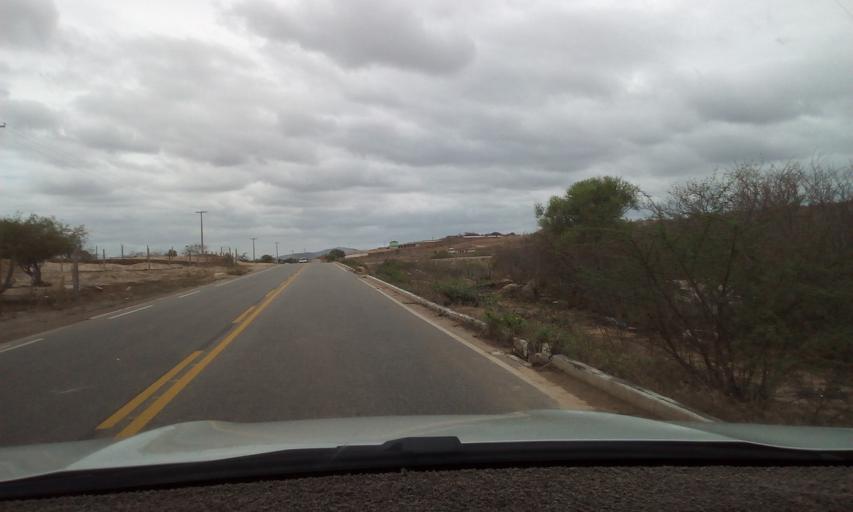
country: BR
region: Paraiba
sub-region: Picui
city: Picui
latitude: -6.5506
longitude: -36.2967
